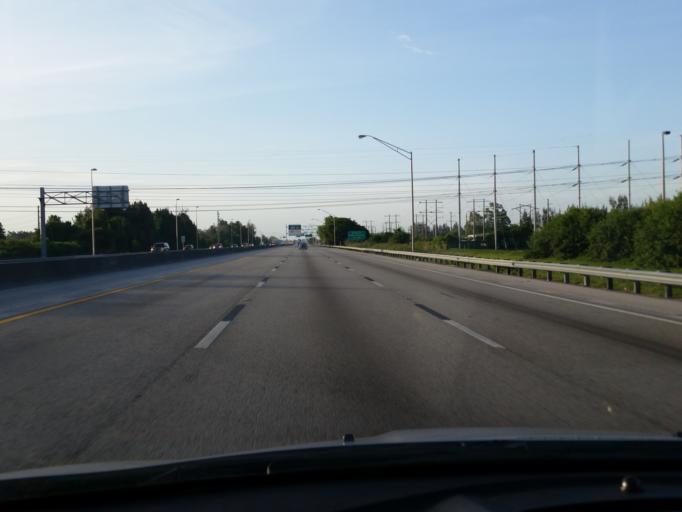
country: US
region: Florida
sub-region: Broward County
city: Davie
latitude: 26.0546
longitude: -80.2150
